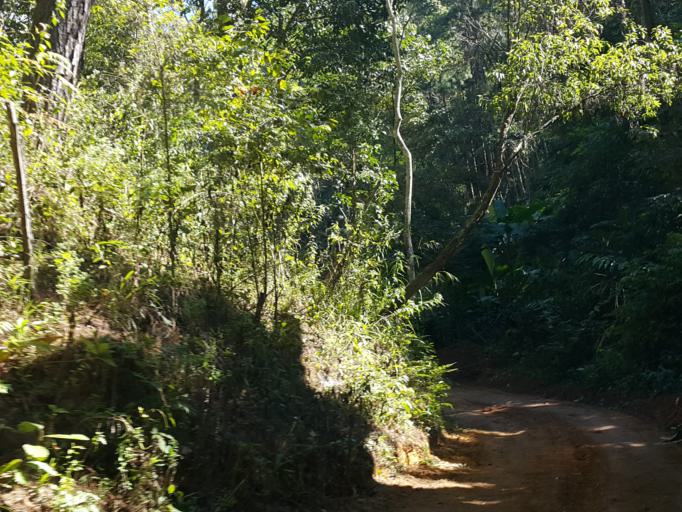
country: TH
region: Chiang Mai
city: Wiang Haeng
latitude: 19.5174
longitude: 98.8120
